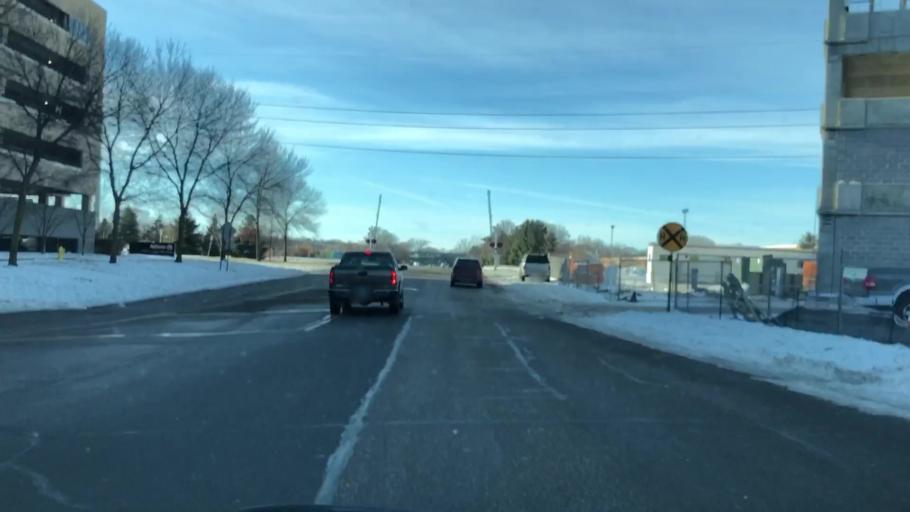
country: US
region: Minnesota
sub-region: Hennepin County
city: Saint Louis Park
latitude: 44.9729
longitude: -93.3536
